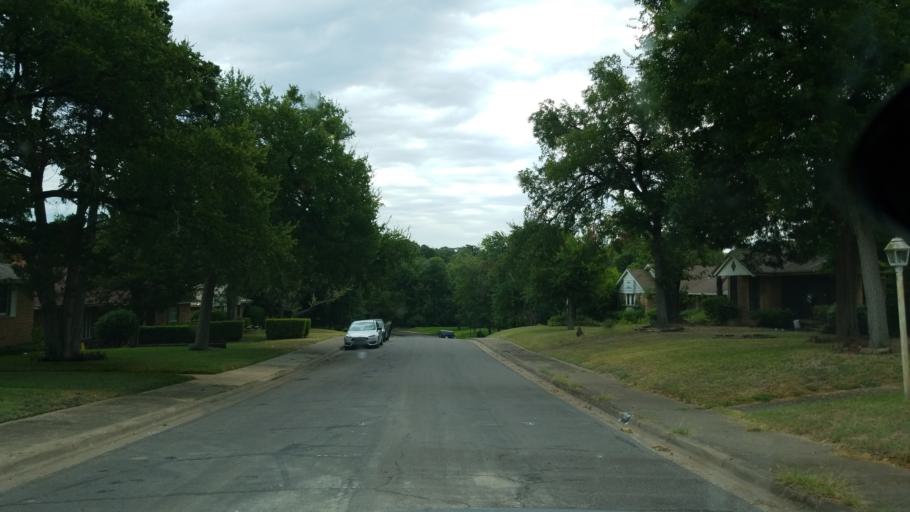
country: US
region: Texas
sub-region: Dallas County
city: Duncanville
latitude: 32.6677
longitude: -96.8384
